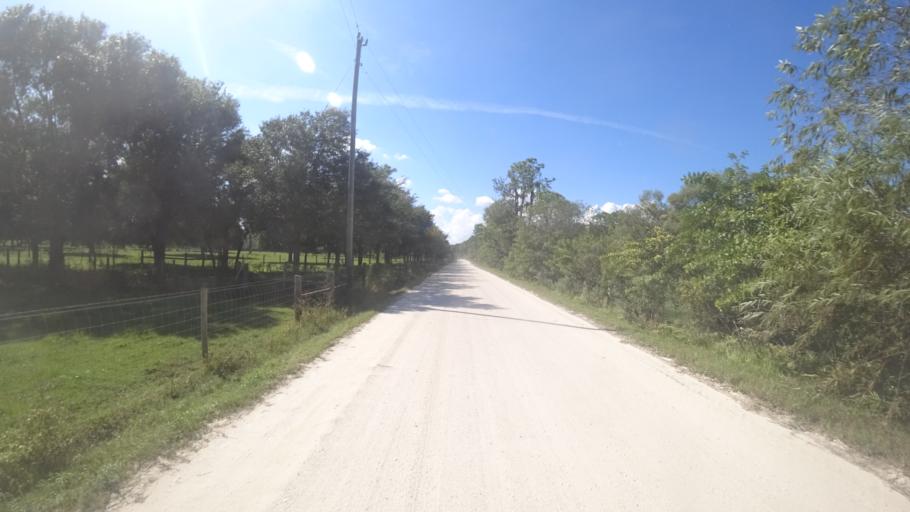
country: US
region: Florida
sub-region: Sarasota County
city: The Meadows
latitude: 27.4526
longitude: -82.2977
